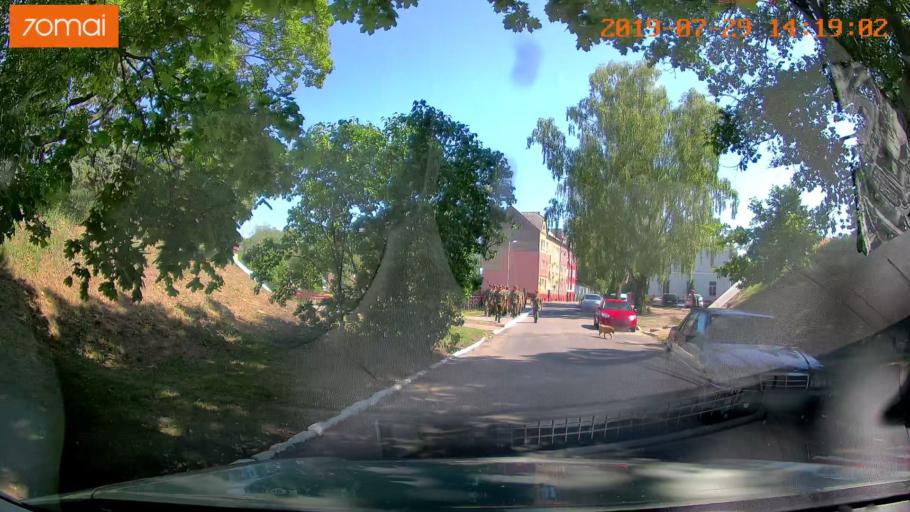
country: RU
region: Kaliningrad
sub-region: Gorod Kaliningrad
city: Baltiysk
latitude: 54.6415
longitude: 19.8895
